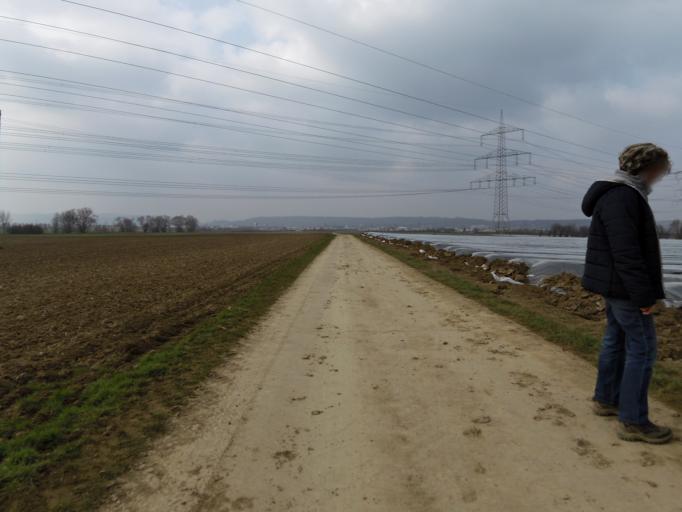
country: DE
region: Rheinland-Pfalz
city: Obersulzen
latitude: 49.5611
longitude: 8.2010
